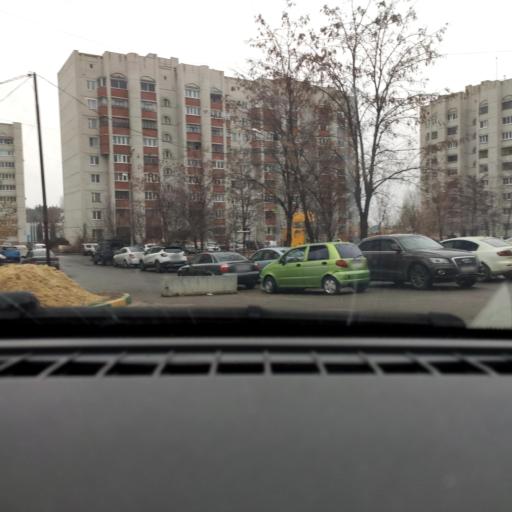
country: RU
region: Voronezj
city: Shilovo
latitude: 51.5605
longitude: 39.1166
